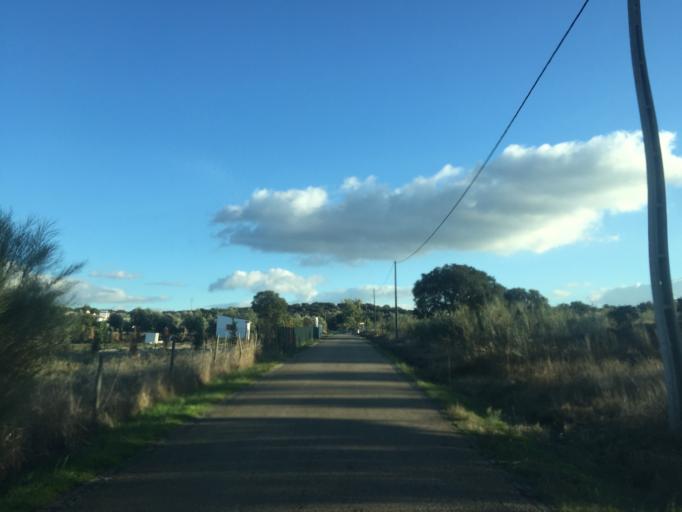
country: PT
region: Portalegre
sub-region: Alter do Chao
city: Alter do Chao
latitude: 39.1886
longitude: -7.6292
